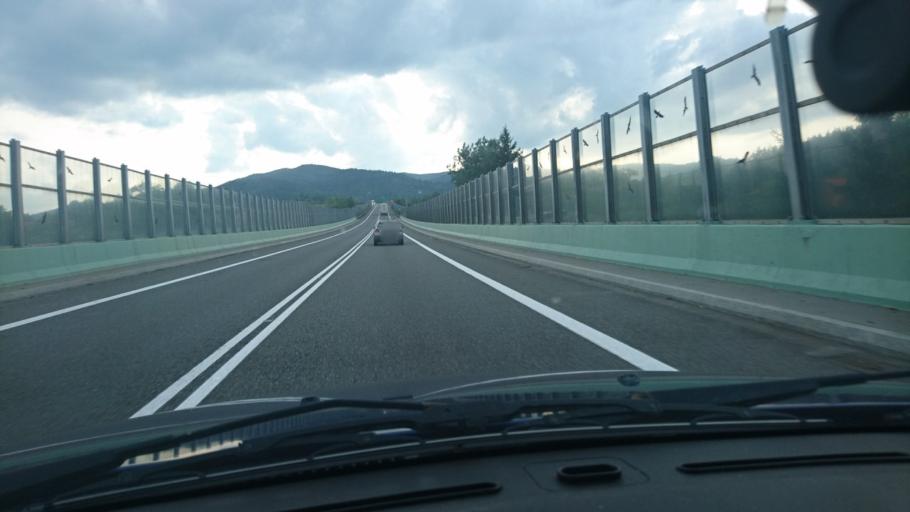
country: PL
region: Silesian Voivodeship
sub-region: Powiat zywiecki
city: Radziechowy
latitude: 49.6287
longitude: 19.1484
